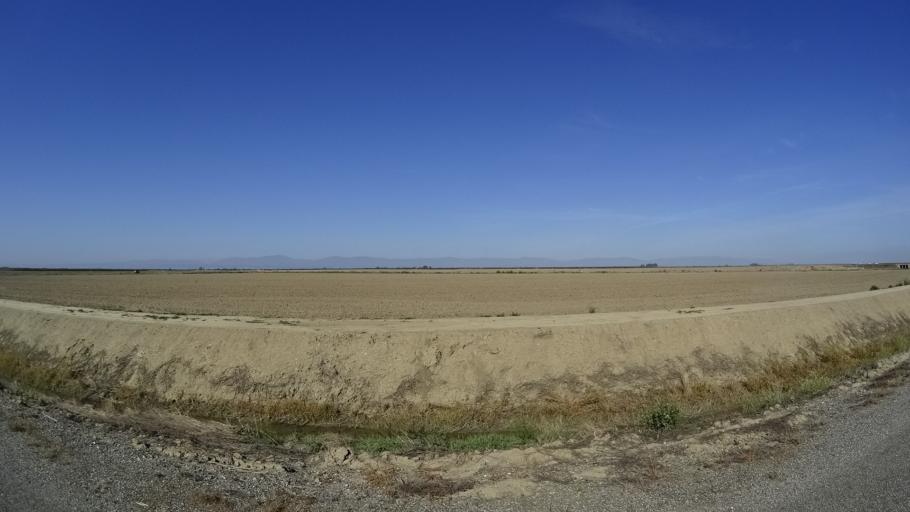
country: US
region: California
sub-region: Glenn County
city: Willows
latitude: 39.5837
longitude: -122.1168
